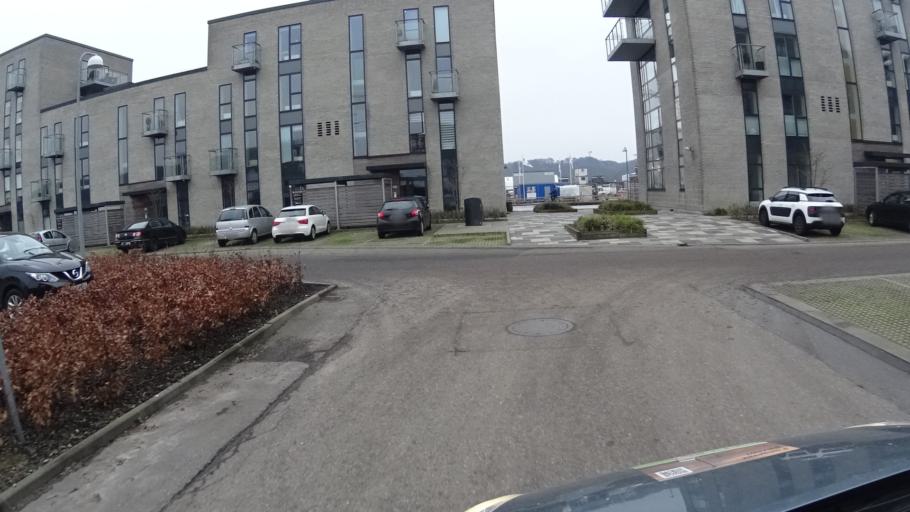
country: DK
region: South Denmark
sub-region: Vejle Kommune
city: Vejle
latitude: 55.7081
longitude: 9.5550
